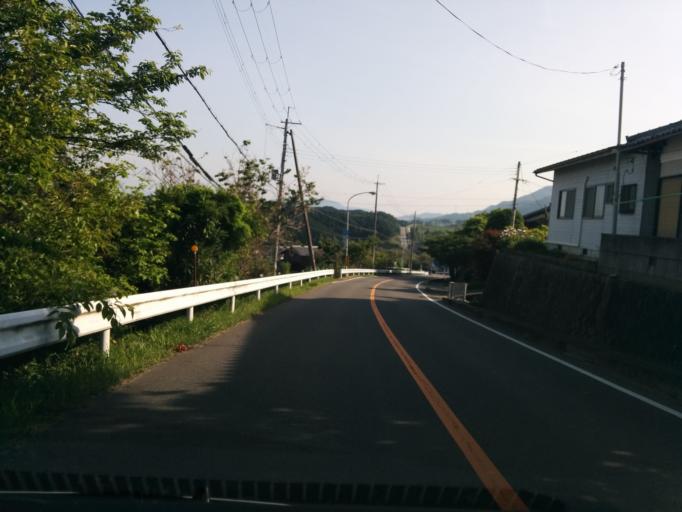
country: JP
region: Shiga Prefecture
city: Kitahama
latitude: 35.1070
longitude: 135.8811
